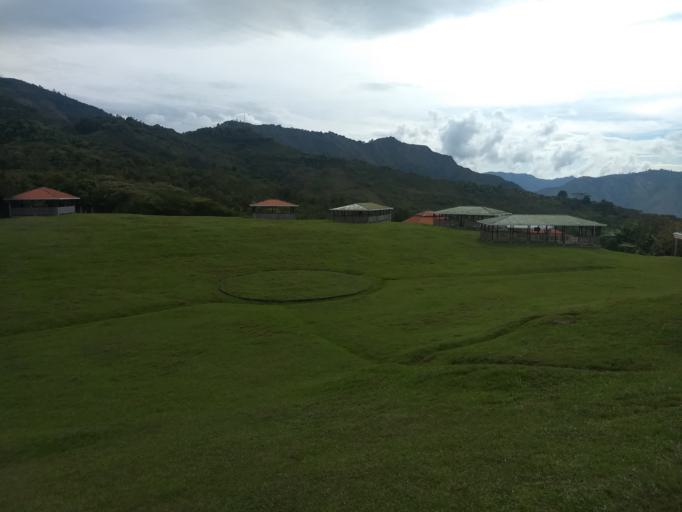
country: CO
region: Cauca
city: Inza
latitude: 2.5739
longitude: -76.0333
